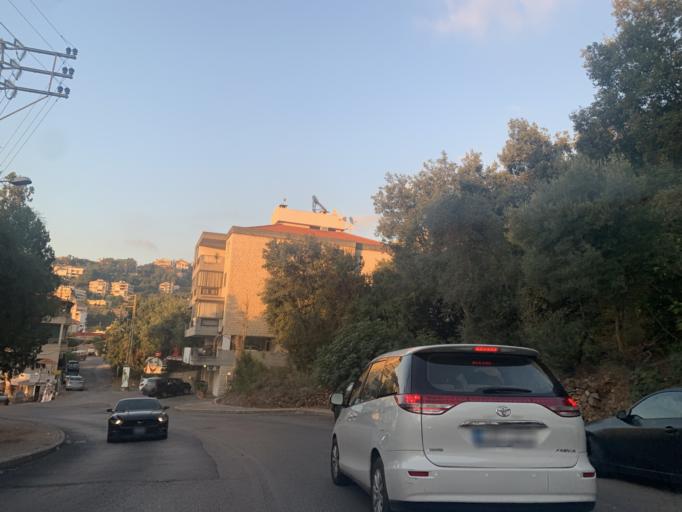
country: LB
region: Mont-Liban
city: Djounie
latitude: 33.9546
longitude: 35.6424
